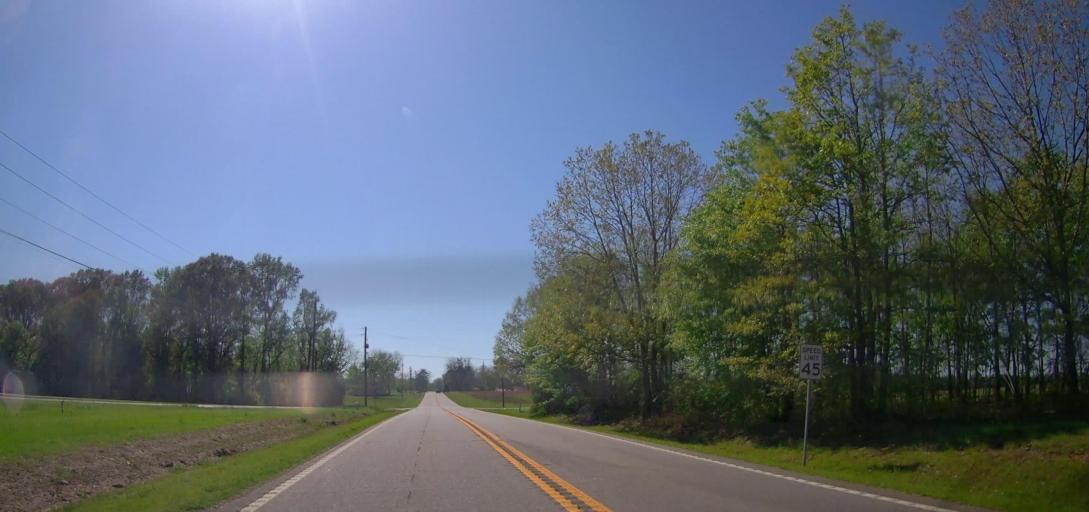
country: US
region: Georgia
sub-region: Dooly County
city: Unadilla
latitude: 32.2603
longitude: -83.7182
